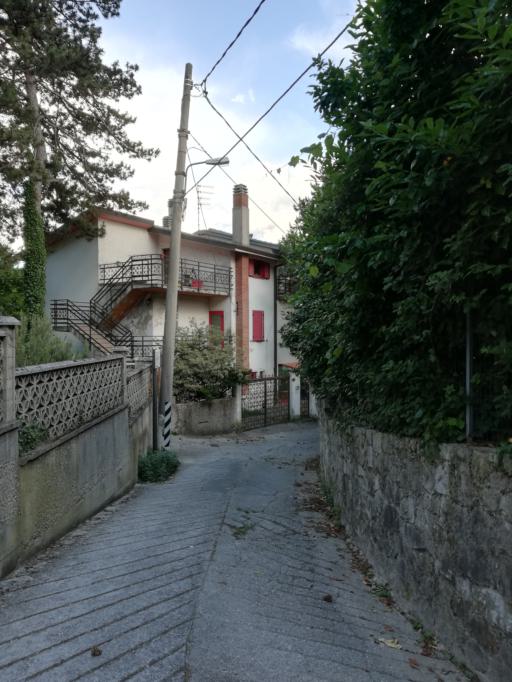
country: IT
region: Friuli Venezia Giulia
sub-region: Provincia di Trieste
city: Villa Opicina
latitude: 45.6672
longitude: 13.8030
